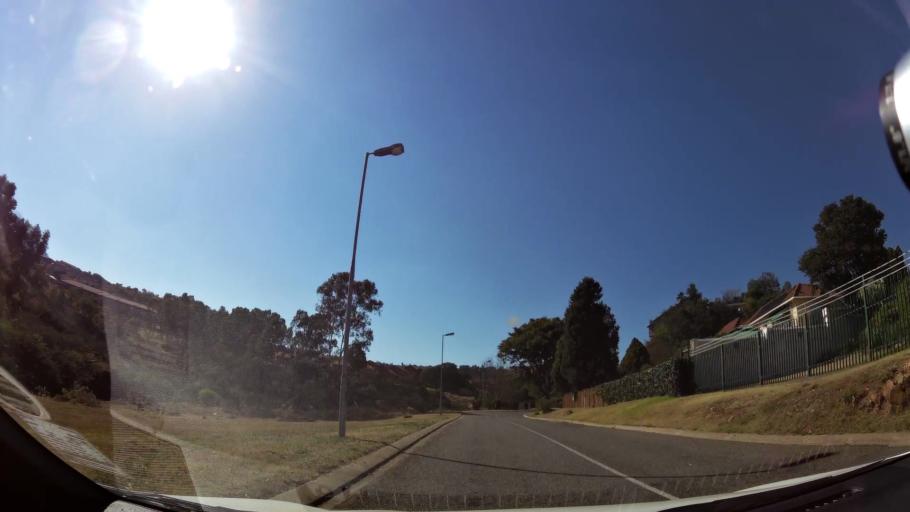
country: ZA
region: Gauteng
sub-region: City of Johannesburg Metropolitan Municipality
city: Johannesburg
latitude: -26.2700
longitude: 28.0106
